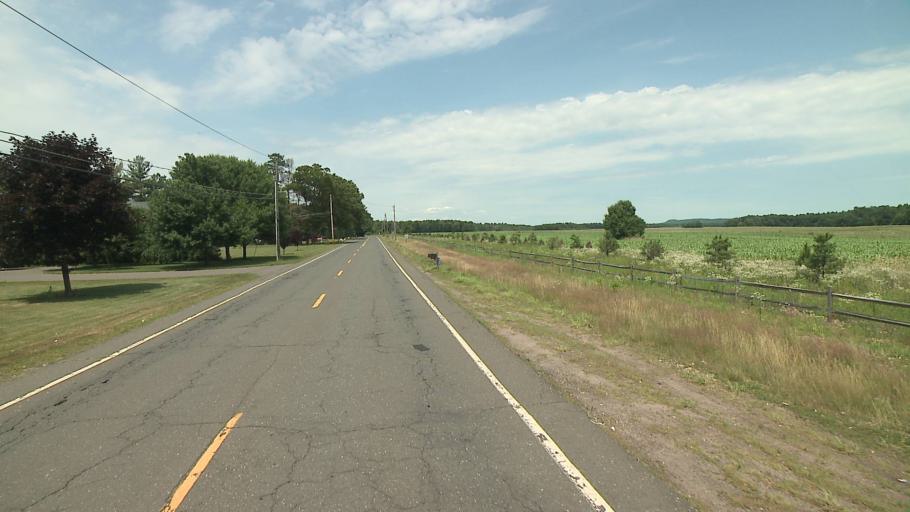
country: US
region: Massachusetts
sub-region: Hampden County
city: Southwick
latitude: 42.0284
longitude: -72.7491
